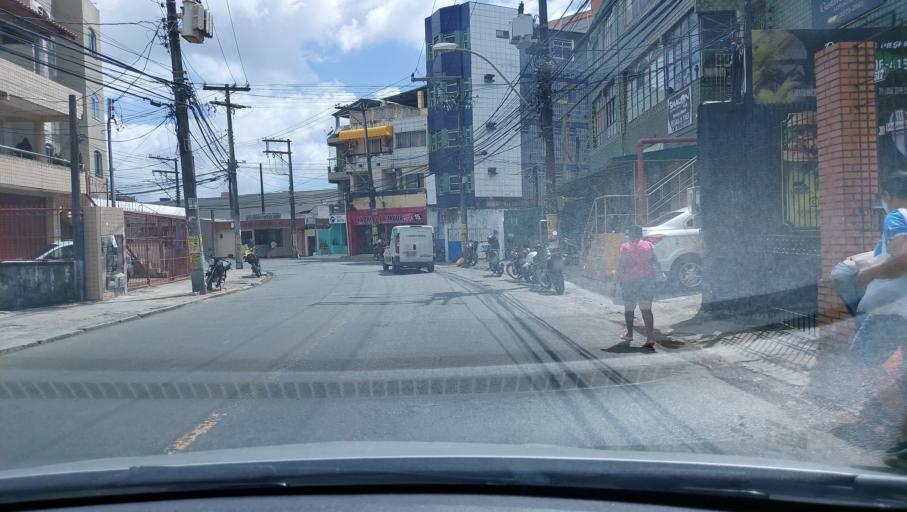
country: BR
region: Bahia
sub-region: Salvador
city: Salvador
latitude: -12.9773
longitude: -38.4955
